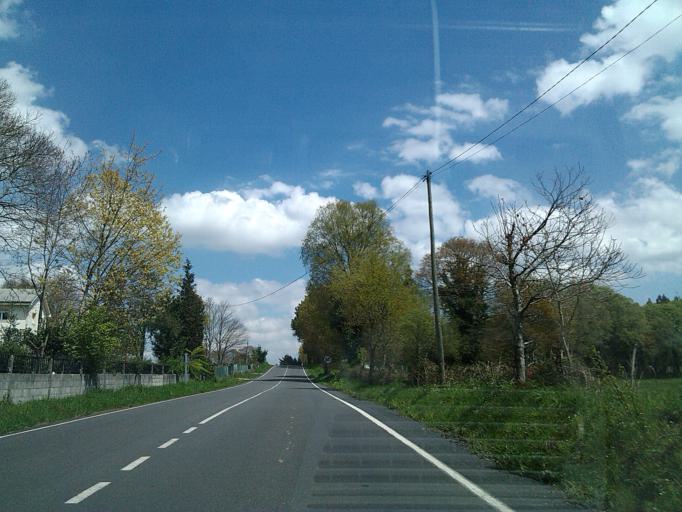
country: ES
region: Galicia
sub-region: Provincia da Coruna
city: Melide
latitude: 42.9466
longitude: -8.0027
